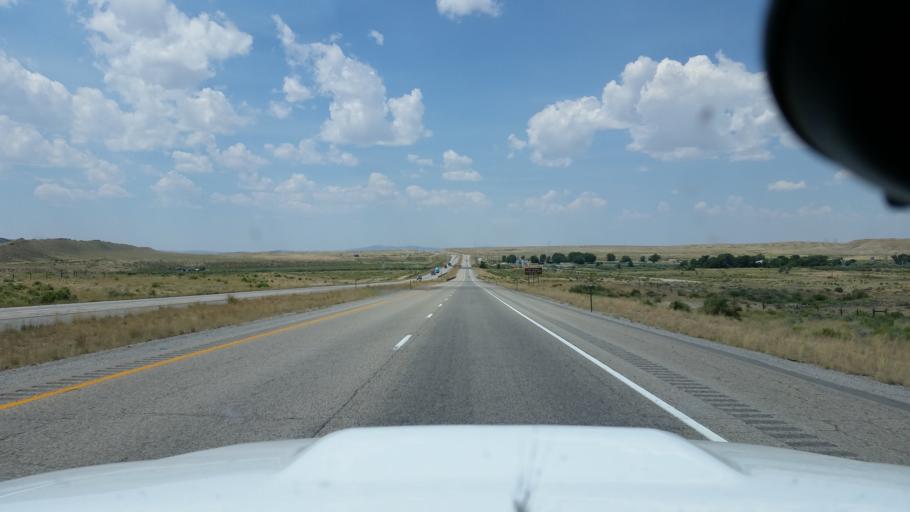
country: US
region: Wyoming
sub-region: Carbon County
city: Rawlins
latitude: 41.7483
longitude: -106.9382
